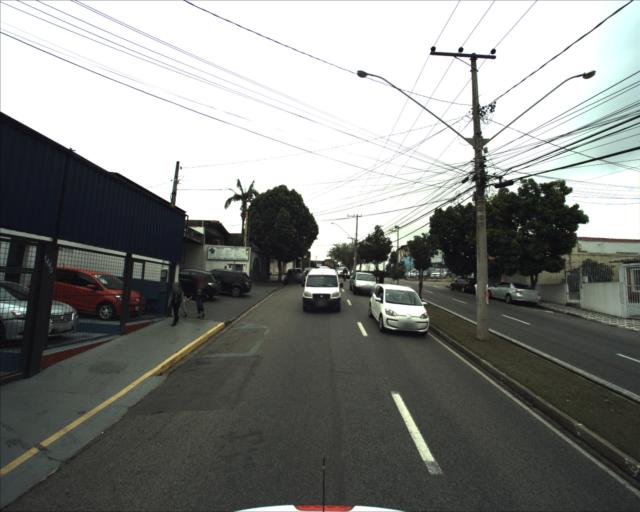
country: BR
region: Sao Paulo
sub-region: Sorocaba
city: Sorocaba
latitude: -23.5176
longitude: -47.4688
